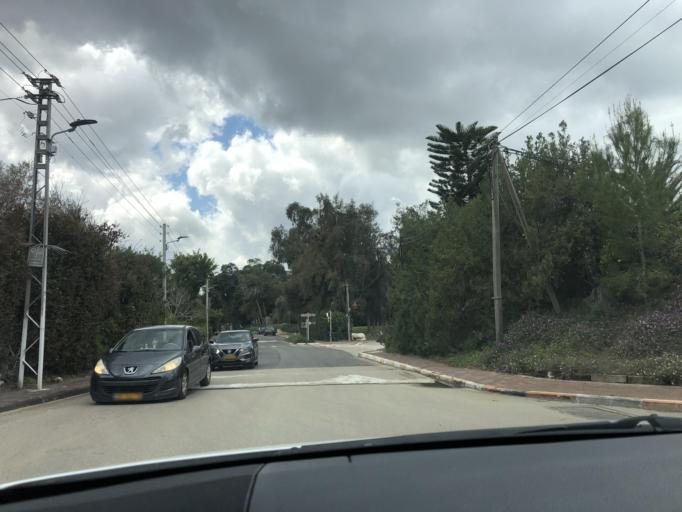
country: IL
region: Central District
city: Tel Mond
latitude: 32.2664
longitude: 34.9338
